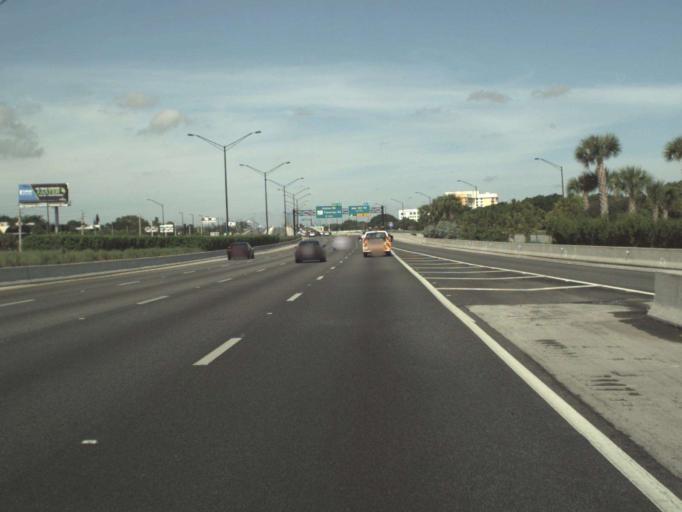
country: US
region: Florida
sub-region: Broward County
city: Pine Island Ridge
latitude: 26.1001
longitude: -80.2543
